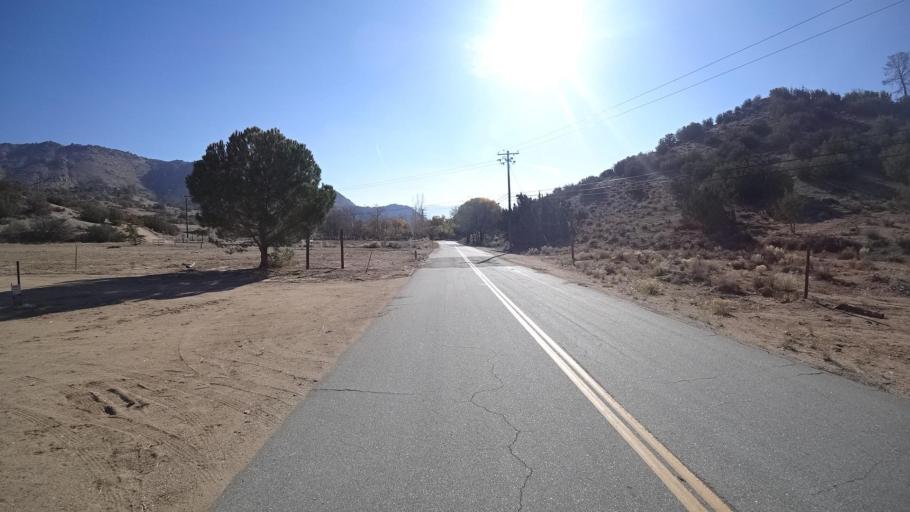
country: US
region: California
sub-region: Kern County
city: Tehachapi
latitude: 35.3653
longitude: -118.3839
